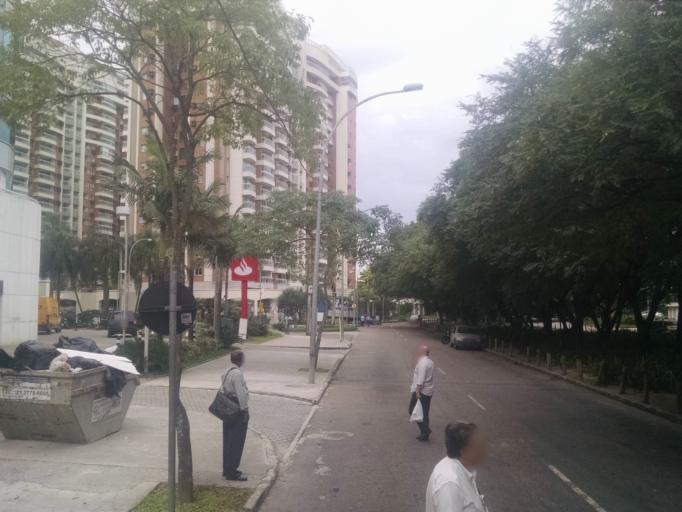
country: BR
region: Rio de Janeiro
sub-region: Rio De Janeiro
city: Rio de Janeiro
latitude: -22.9883
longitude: -43.3582
